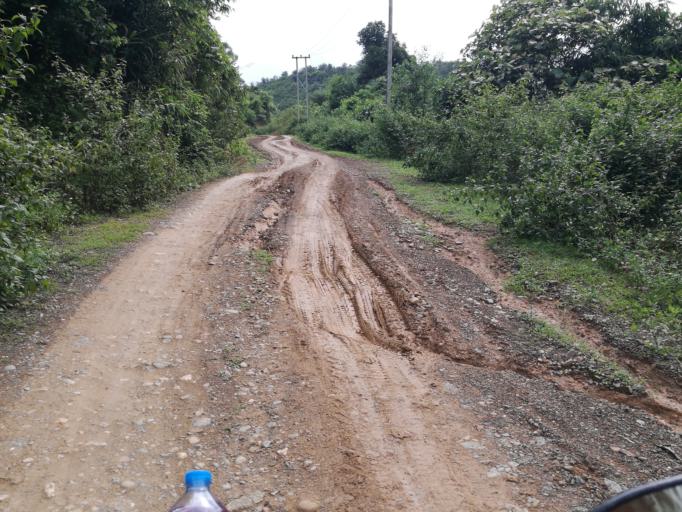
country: LA
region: Phongsali
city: Khoa
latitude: 21.2322
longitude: 102.6909
